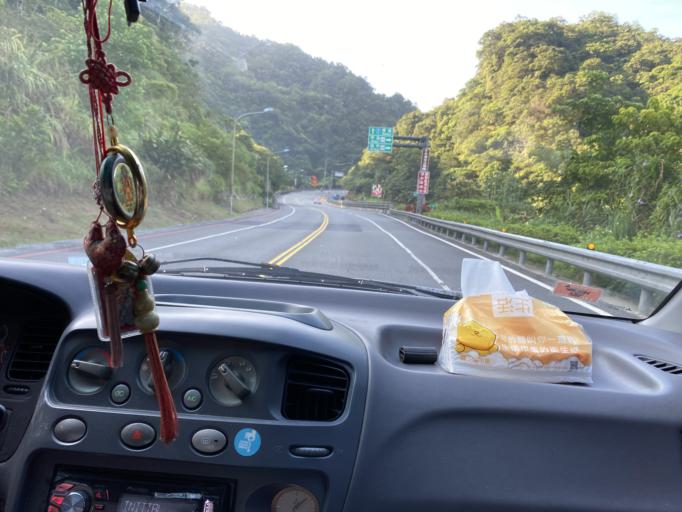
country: TW
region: Taiwan
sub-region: Keelung
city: Keelung
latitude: 25.0405
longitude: 121.7798
